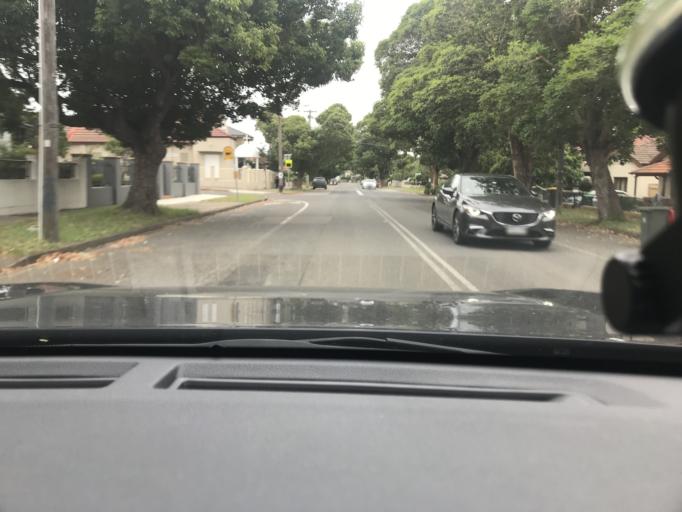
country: AU
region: New South Wales
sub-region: Canada Bay
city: Concord
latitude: -33.8615
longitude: 151.1093
